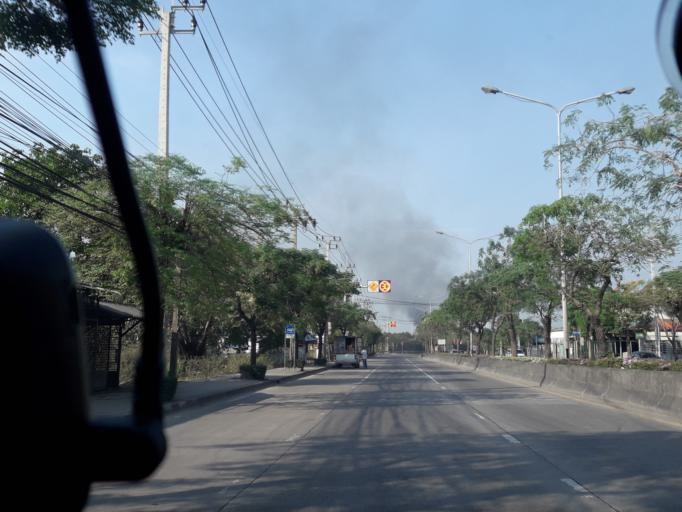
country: TH
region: Pathum Thani
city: Lam Luk Ka
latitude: 13.8907
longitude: 100.7317
